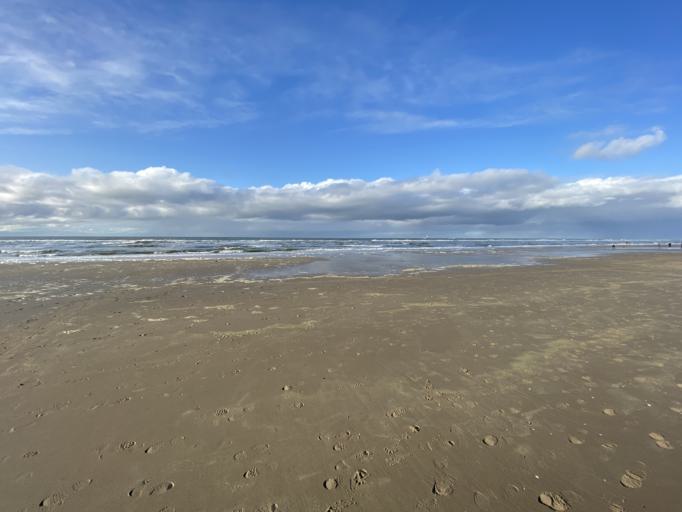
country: NL
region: North Holland
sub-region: Gemeente Texel
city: Den Burg
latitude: 53.1037
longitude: 4.7555
